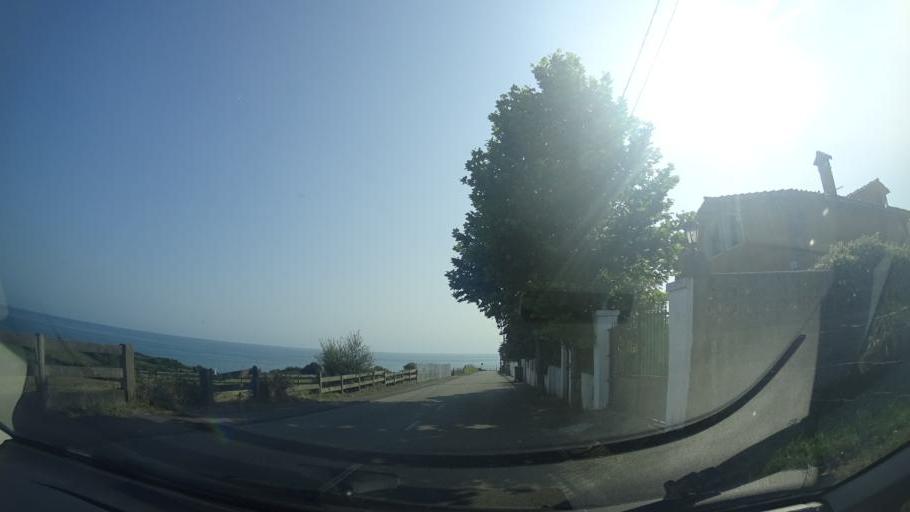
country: ES
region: Asturias
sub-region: Province of Asturias
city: Colunga
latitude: 43.4718
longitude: -5.1872
